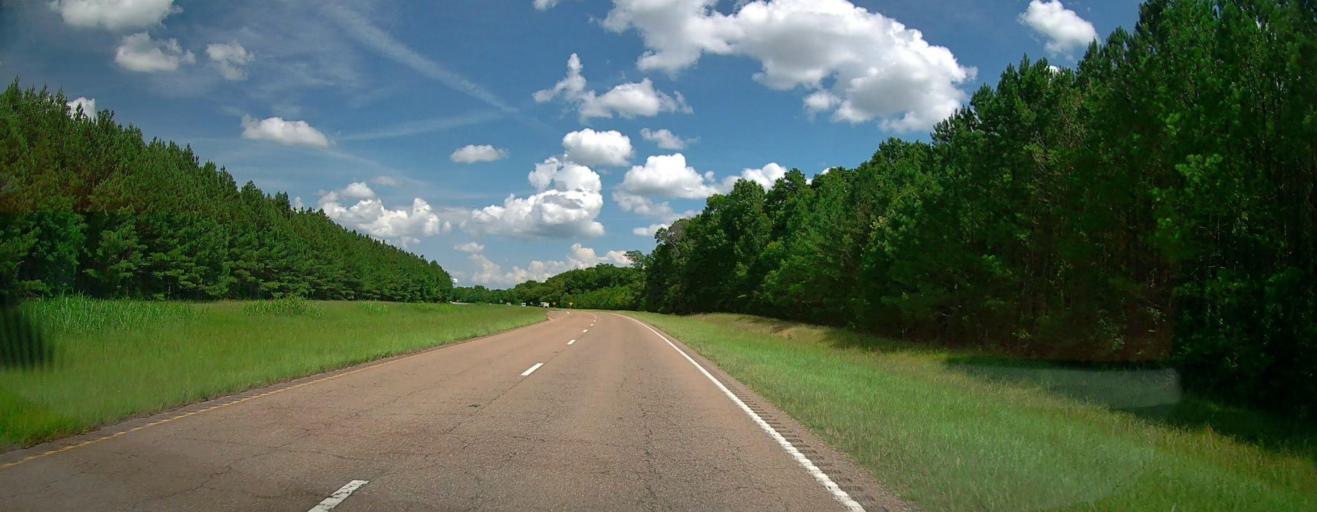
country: US
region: Mississippi
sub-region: Monroe County
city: Aberdeen
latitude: 33.8166
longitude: -88.5775
